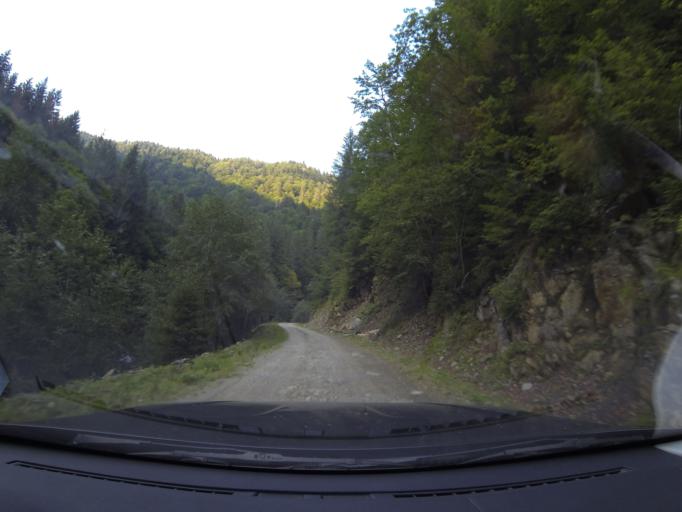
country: RO
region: Arges
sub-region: Comuna Arefu
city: Arefu
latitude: 45.5139
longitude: 24.6695
